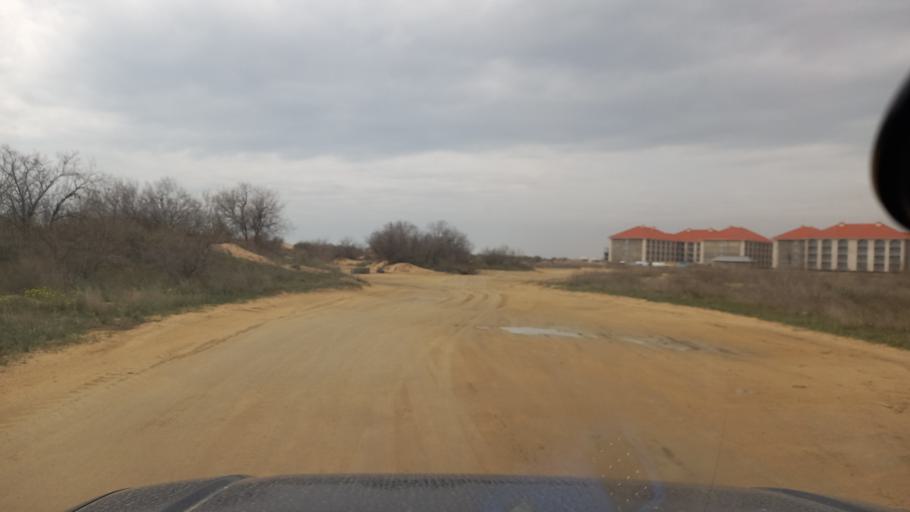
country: RU
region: Krasnodarskiy
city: Vityazevo
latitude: 44.9925
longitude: 37.2370
